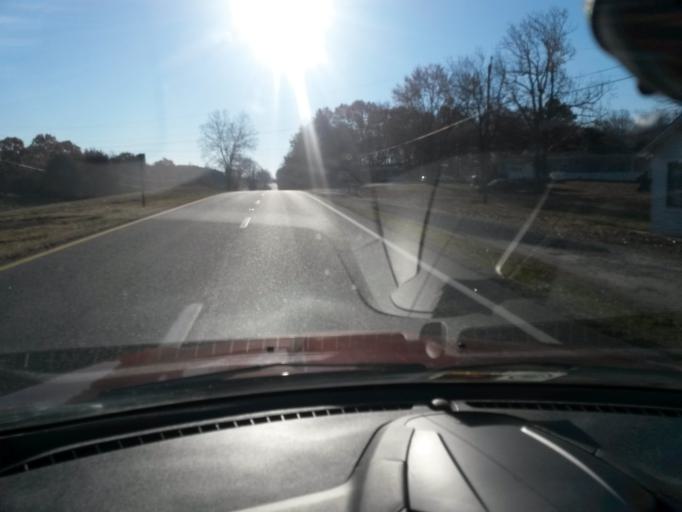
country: US
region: Virginia
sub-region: Appomattox County
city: Appomattox
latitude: 37.2973
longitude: -78.7401
